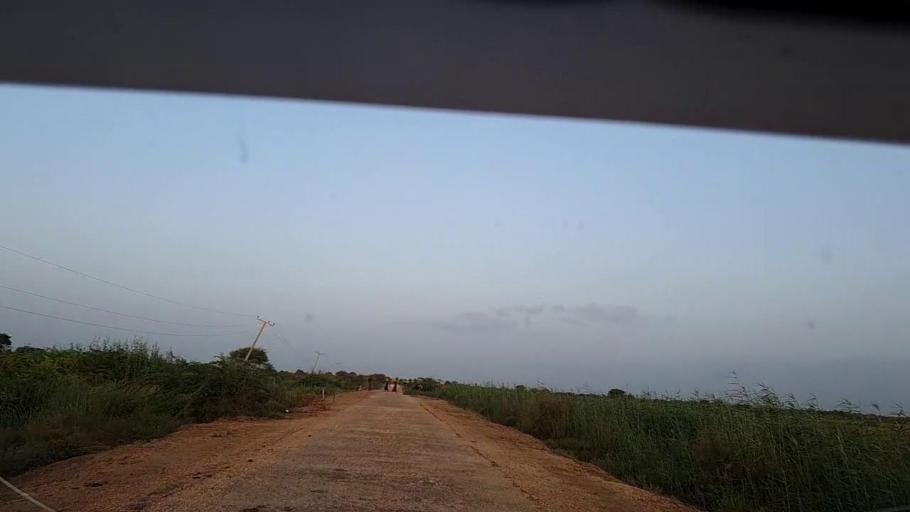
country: PK
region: Sindh
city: Kadhan
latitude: 24.5293
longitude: 68.9486
